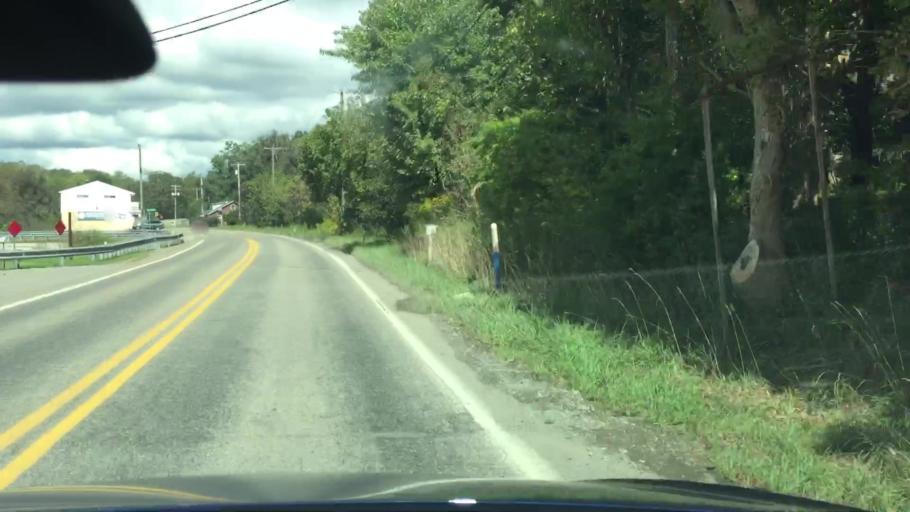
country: US
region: Pennsylvania
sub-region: Allegheny County
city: Russellton
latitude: 40.6194
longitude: -79.8336
